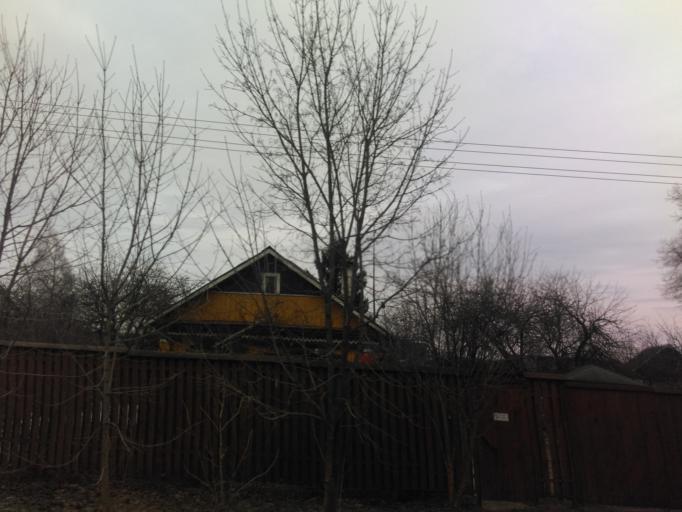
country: RU
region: Moskovskaya
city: Kolyubakino
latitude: 55.6382
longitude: 36.5404
